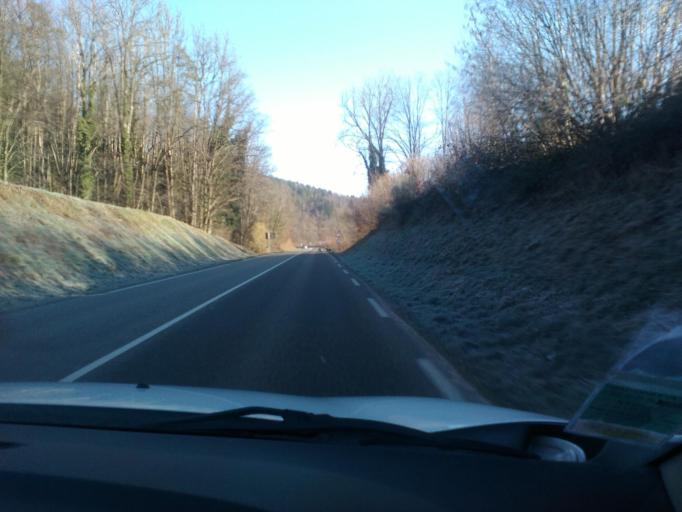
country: FR
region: Alsace
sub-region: Departement du Bas-Rhin
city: Rothau
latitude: 48.4369
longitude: 7.1834
